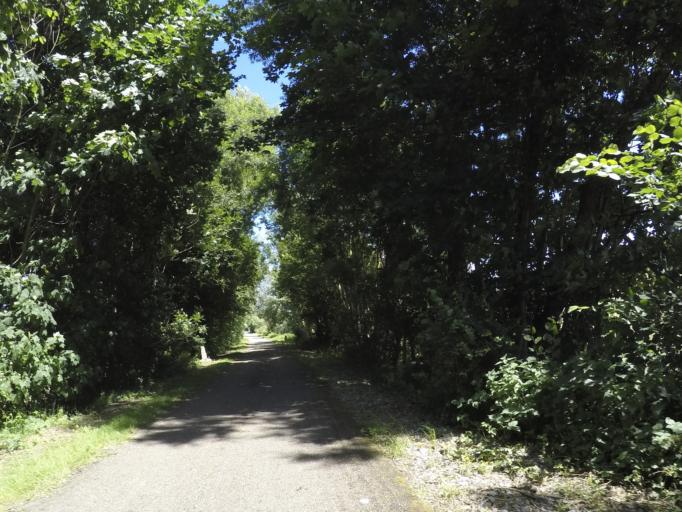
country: BE
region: Wallonia
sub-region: Province de Namur
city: Ciney
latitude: 50.3138
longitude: 5.1020
